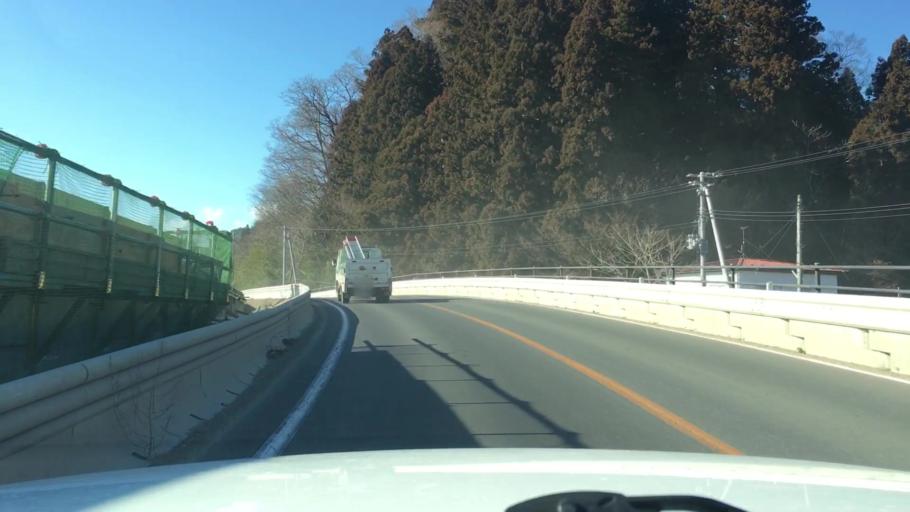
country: JP
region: Iwate
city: Miyako
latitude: 39.6322
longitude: 141.8902
